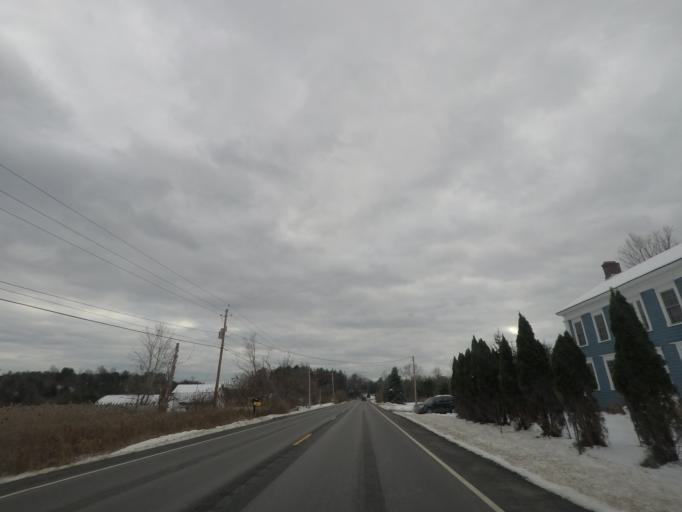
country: US
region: New York
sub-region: Rensselaer County
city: West Sand Lake
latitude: 42.6226
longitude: -73.6034
